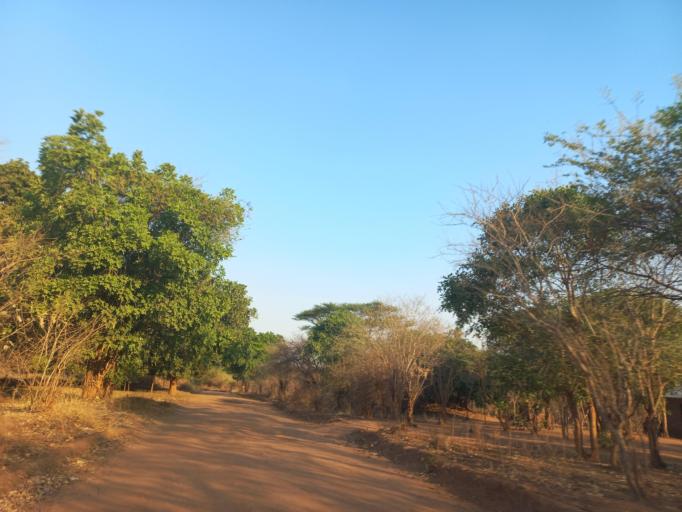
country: ZM
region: Lusaka
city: Luangwa
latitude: -15.4359
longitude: 30.3515
